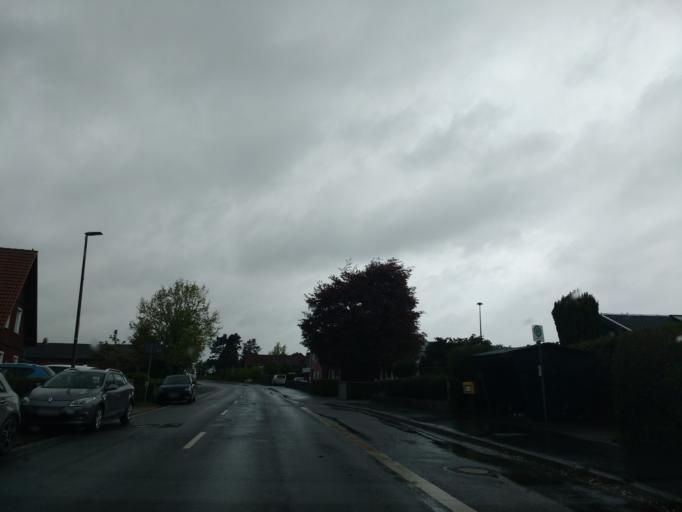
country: DE
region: Schleswig-Holstein
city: Waabs
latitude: 54.5524
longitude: 9.9914
